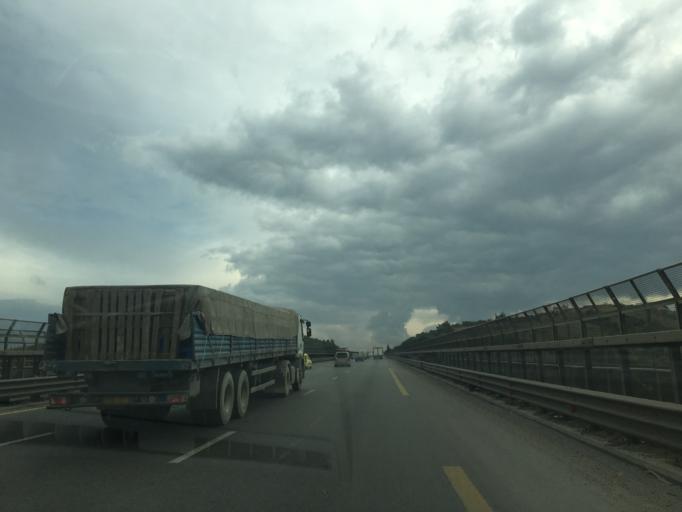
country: DZ
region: Bouira
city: Bouira
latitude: 36.3422
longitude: 3.9227
